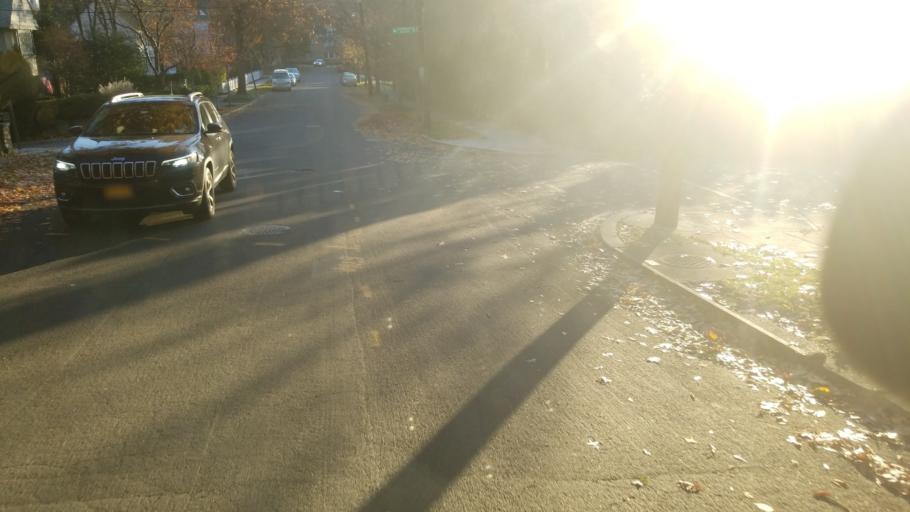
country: US
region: Maryland
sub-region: Montgomery County
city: Friendship Village
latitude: 38.9289
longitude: -77.0854
